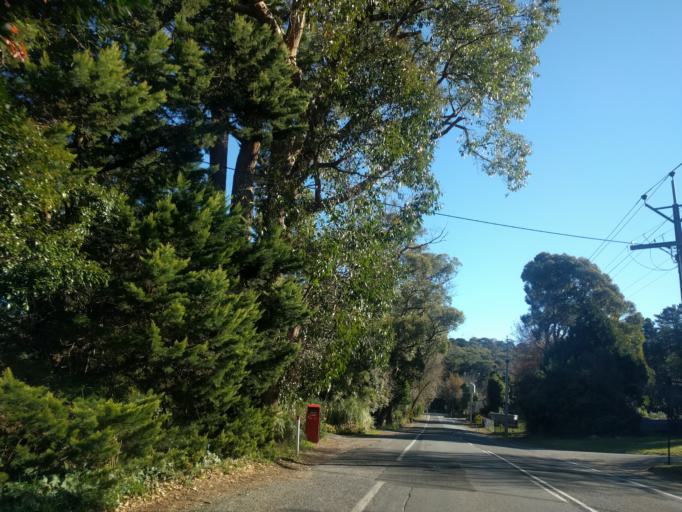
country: AU
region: South Australia
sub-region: Adelaide Hills
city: Crafers
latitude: -34.9941
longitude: 138.7153
